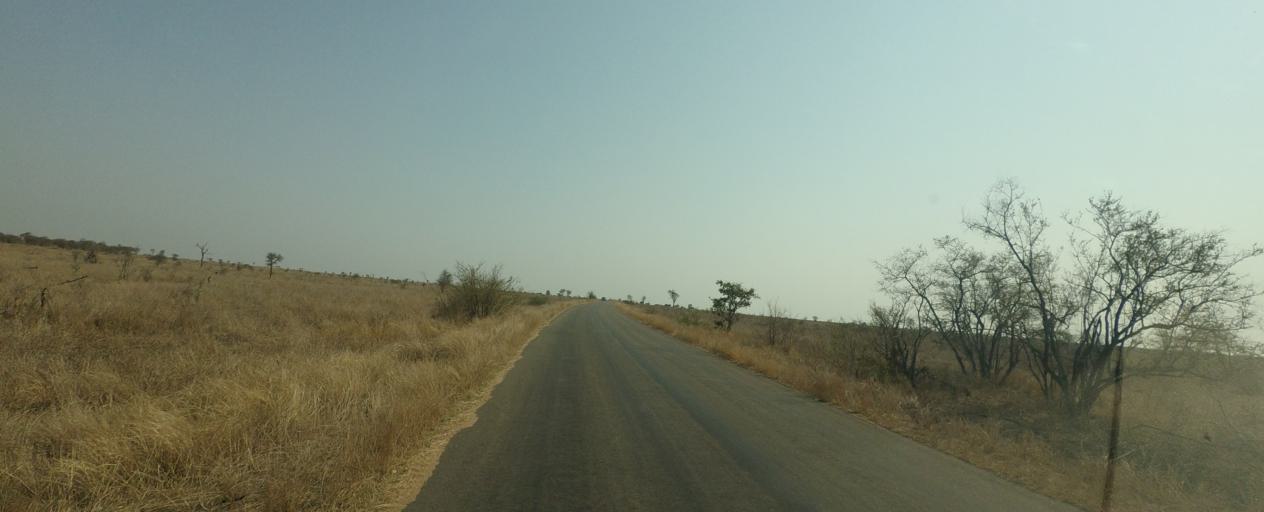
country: ZA
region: Limpopo
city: Thulamahashi
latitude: -24.3603
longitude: 31.7636
